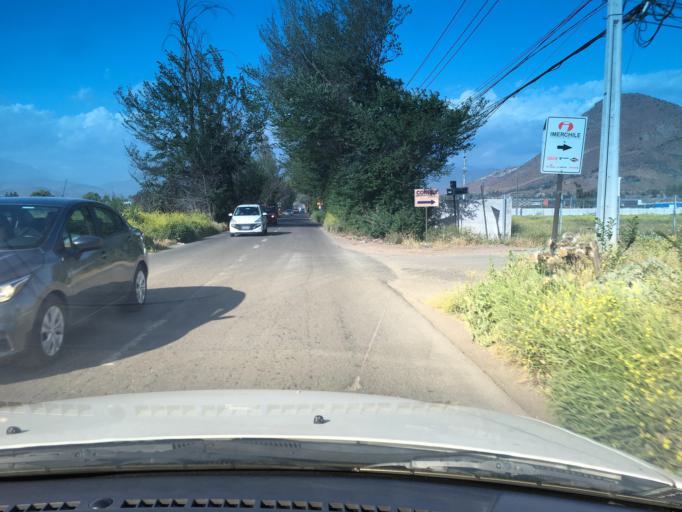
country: CL
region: Santiago Metropolitan
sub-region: Provincia de Chacabuco
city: Chicureo Abajo
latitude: -33.3118
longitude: -70.7195
